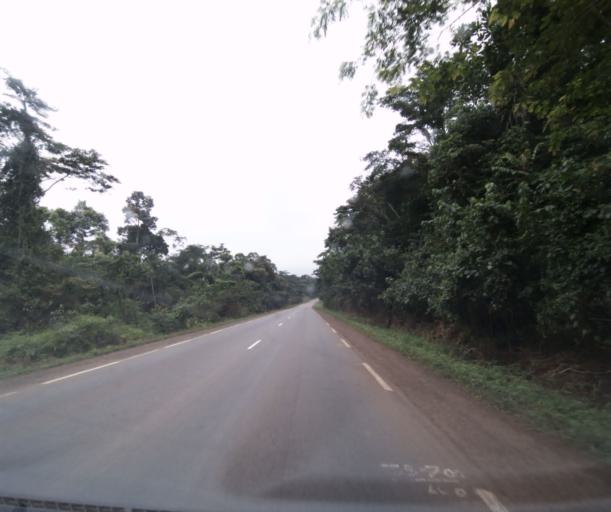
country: CM
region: Centre
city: Mbankomo
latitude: 3.7689
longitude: 11.1830
